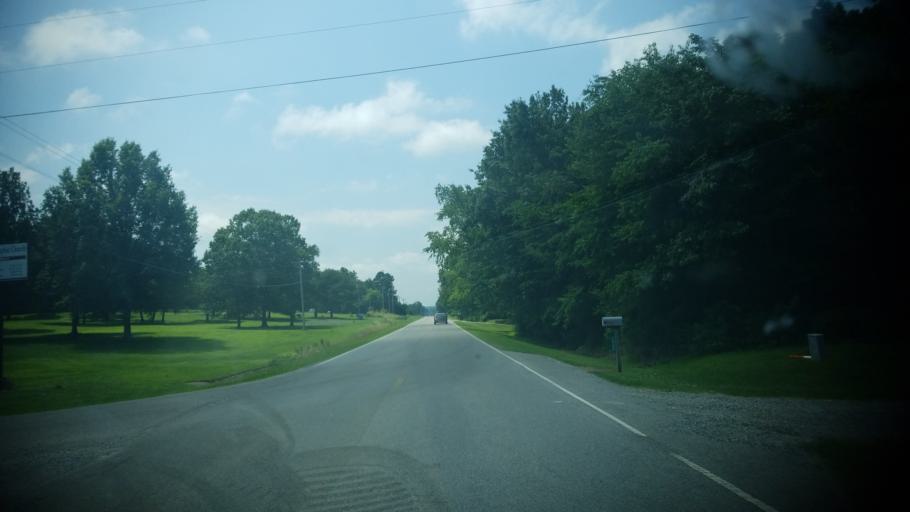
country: US
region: Illinois
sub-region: Wayne County
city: Fairfield
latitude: 38.4084
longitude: -88.3503
